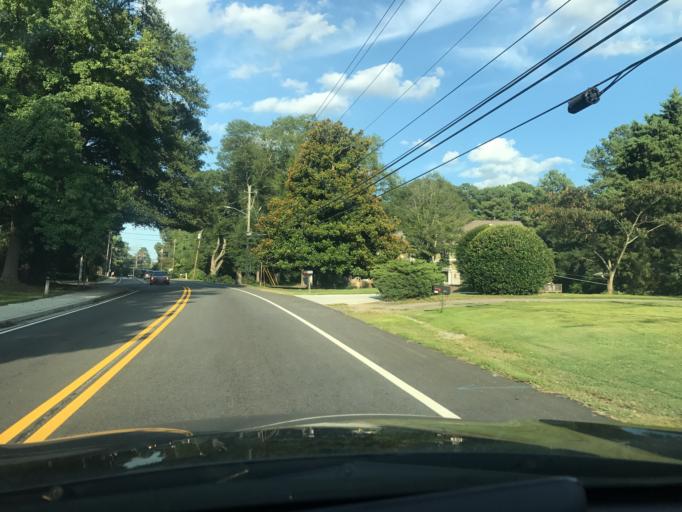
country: US
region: Georgia
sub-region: DeKalb County
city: North Druid Hills
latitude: 33.8226
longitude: -84.2989
